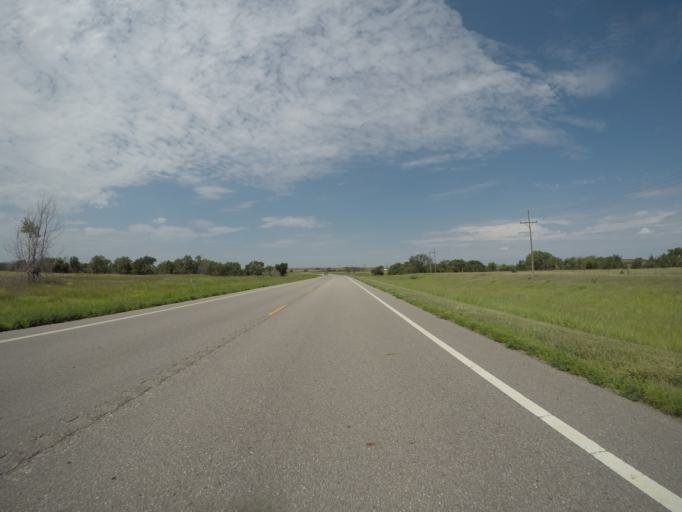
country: US
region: Kansas
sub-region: Rooks County
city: Stockton
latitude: 39.4450
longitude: -99.2326
